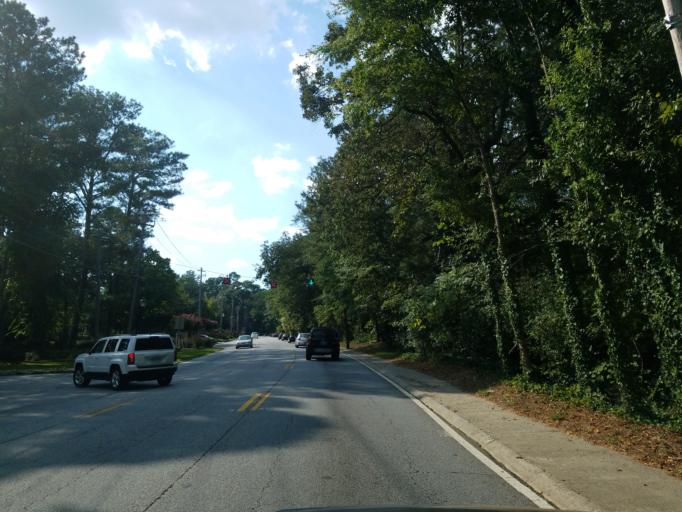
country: US
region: Georgia
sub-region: Fulton County
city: Roswell
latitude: 34.0074
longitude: -84.3529
